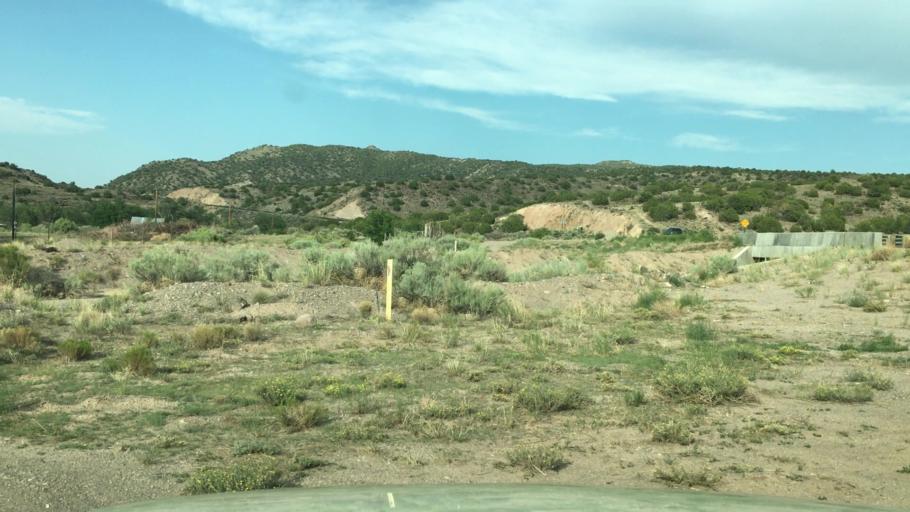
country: US
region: New Mexico
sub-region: Rio Arriba County
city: Chimayo
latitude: 36.2188
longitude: -105.8710
